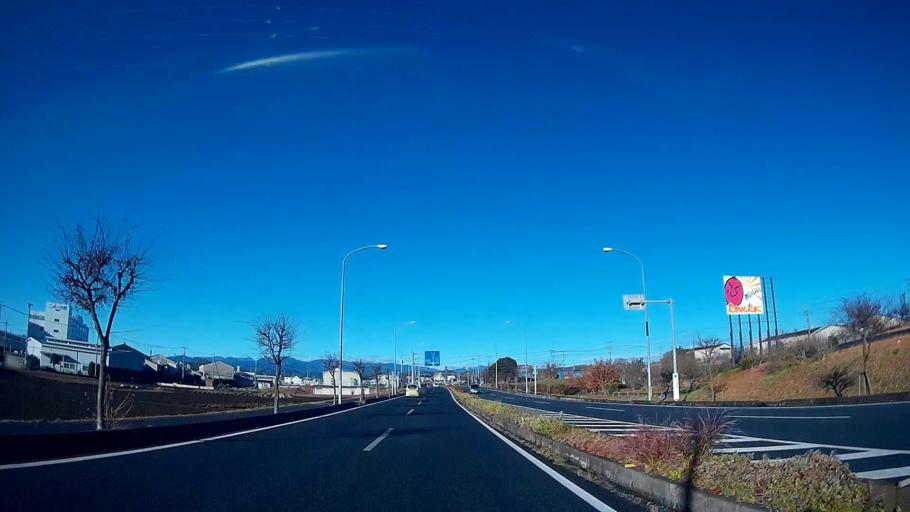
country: JP
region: Saitama
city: Hanno
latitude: 35.8580
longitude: 139.3412
